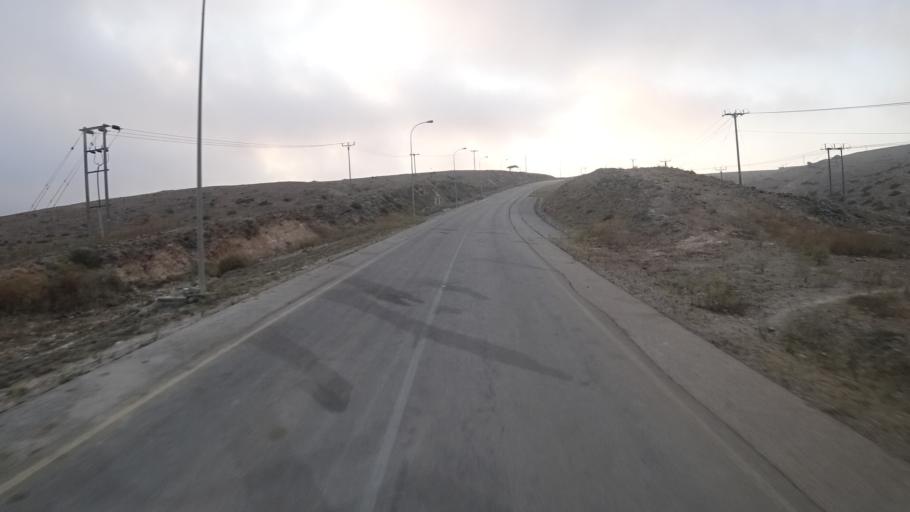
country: OM
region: Zufar
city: Salalah
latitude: 17.1207
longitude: 53.9320
